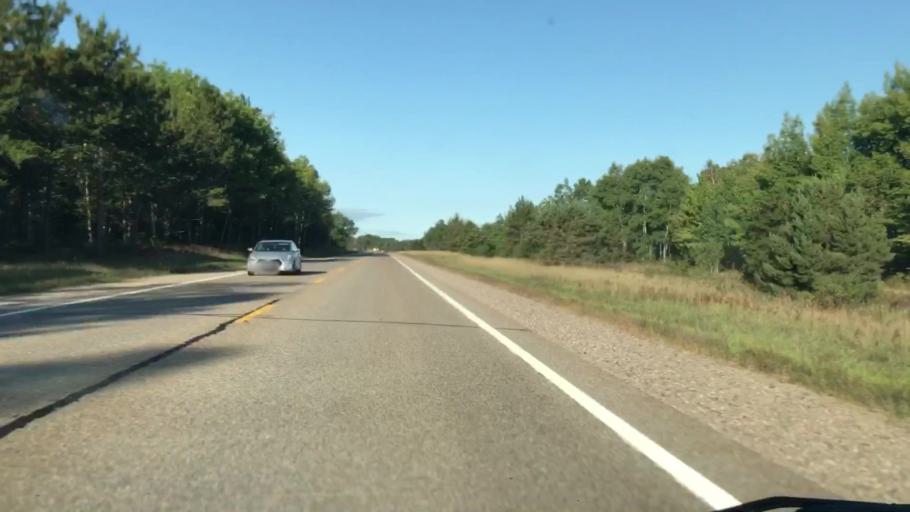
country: US
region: Michigan
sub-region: Mackinac County
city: Saint Ignace
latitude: 46.3584
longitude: -84.8711
